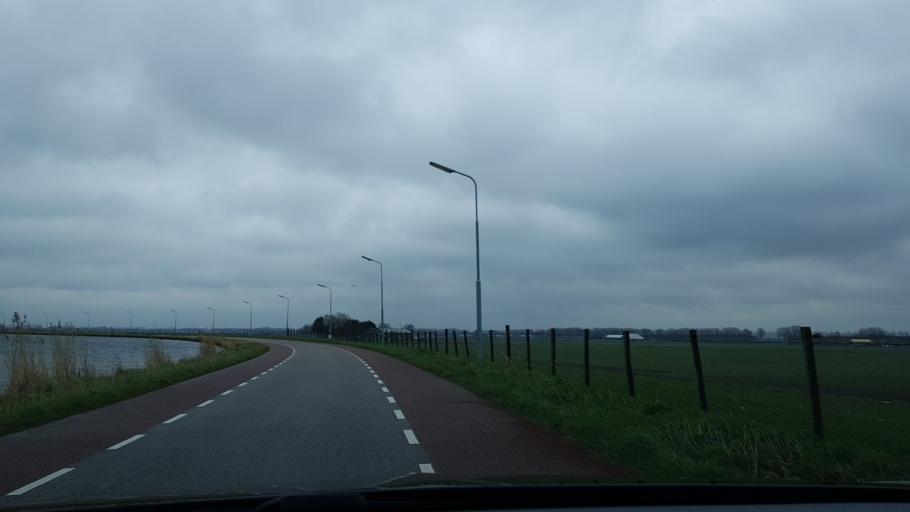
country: NL
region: South Holland
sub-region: Gemeente Lisse
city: Lisse
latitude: 52.2325
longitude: 4.5602
